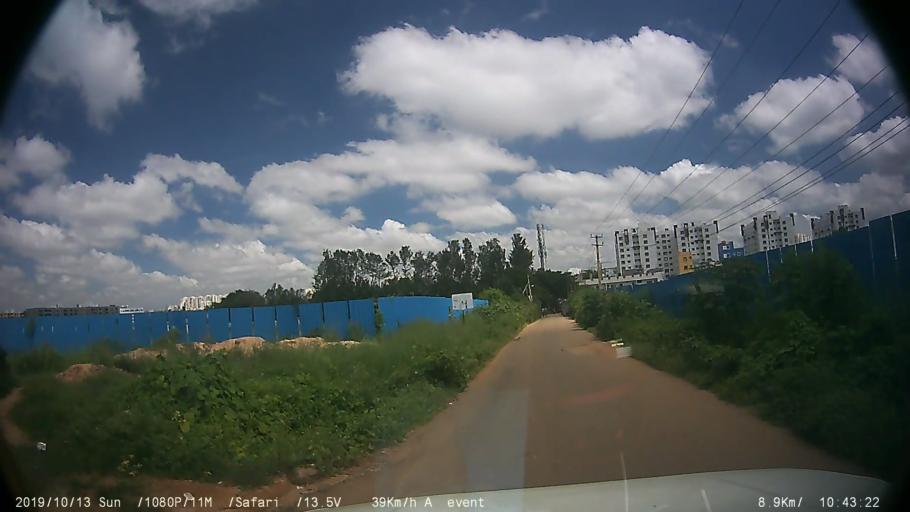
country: IN
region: Karnataka
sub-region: Bangalore Urban
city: Anekal
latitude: 12.8255
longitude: 77.6543
